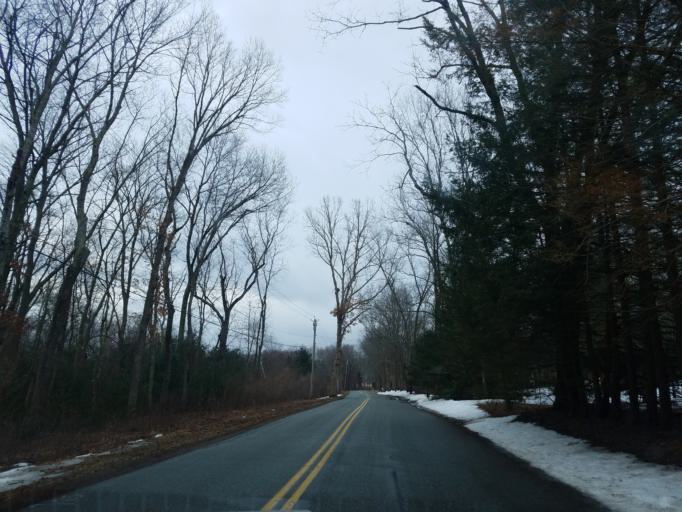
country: US
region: Connecticut
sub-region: Hartford County
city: Glastonbury Center
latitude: 41.6671
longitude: -72.5477
